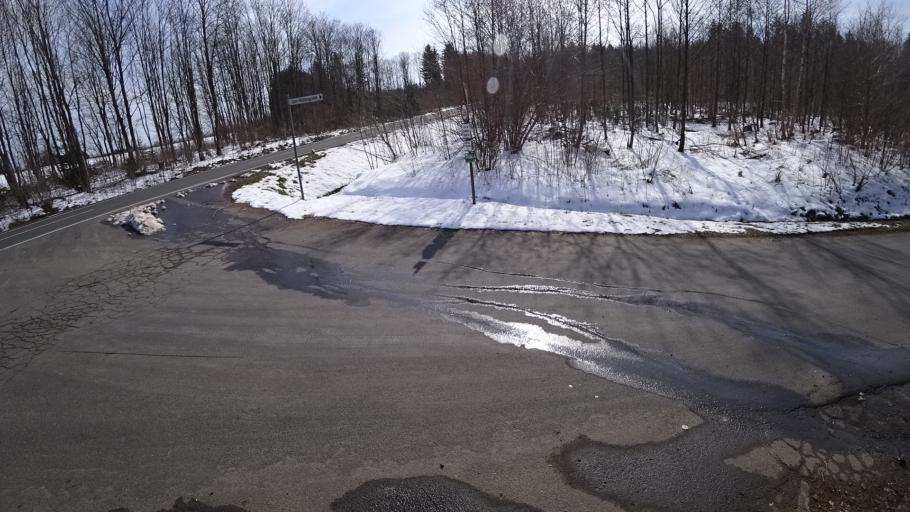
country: DE
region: Rheinland-Pfalz
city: Morlen
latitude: 50.6924
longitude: 7.8880
